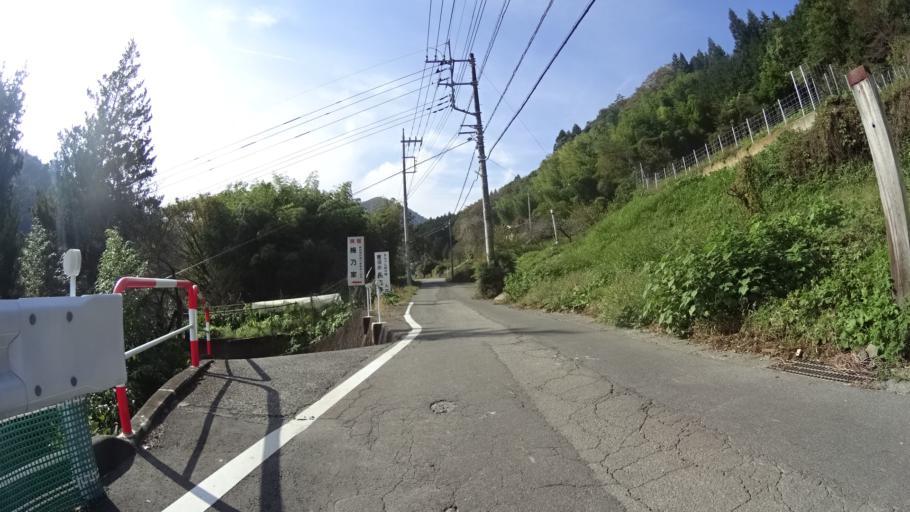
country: JP
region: Yamanashi
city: Otsuki
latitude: 35.5932
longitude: 138.9671
